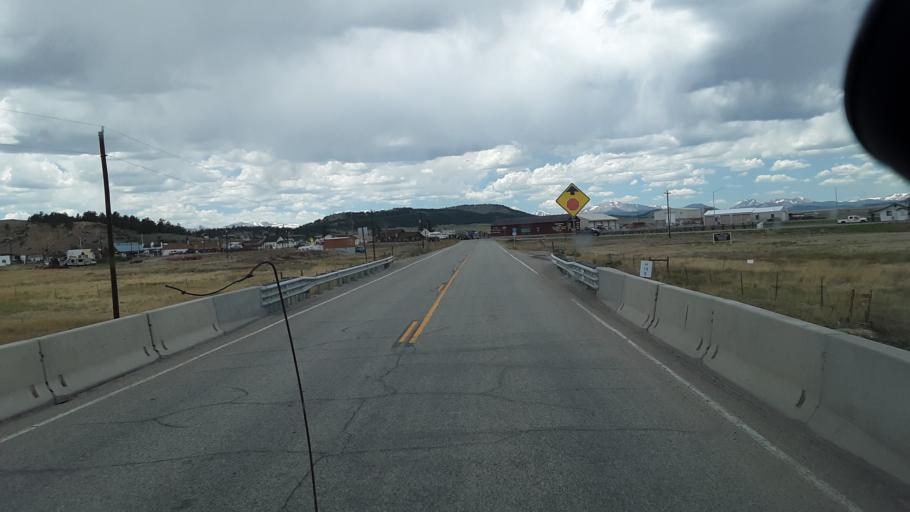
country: US
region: Colorado
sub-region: Park County
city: Fairplay
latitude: 39.0198
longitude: -105.7921
